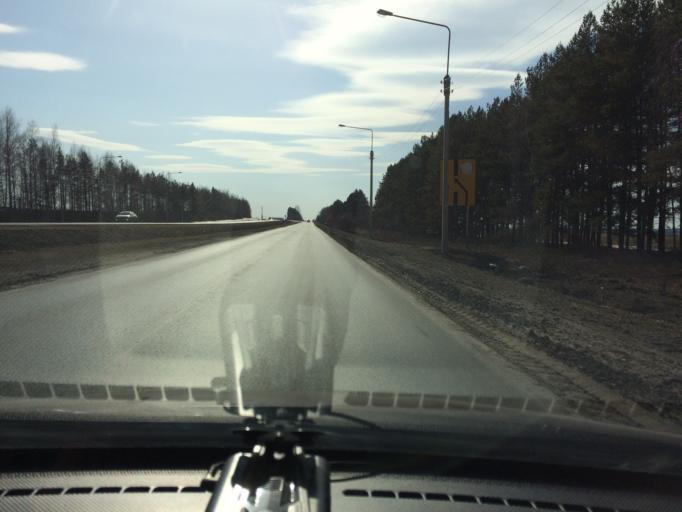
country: RU
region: Mariy-El
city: Yoshkar-Ola
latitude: 56.7223
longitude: 48.1123
